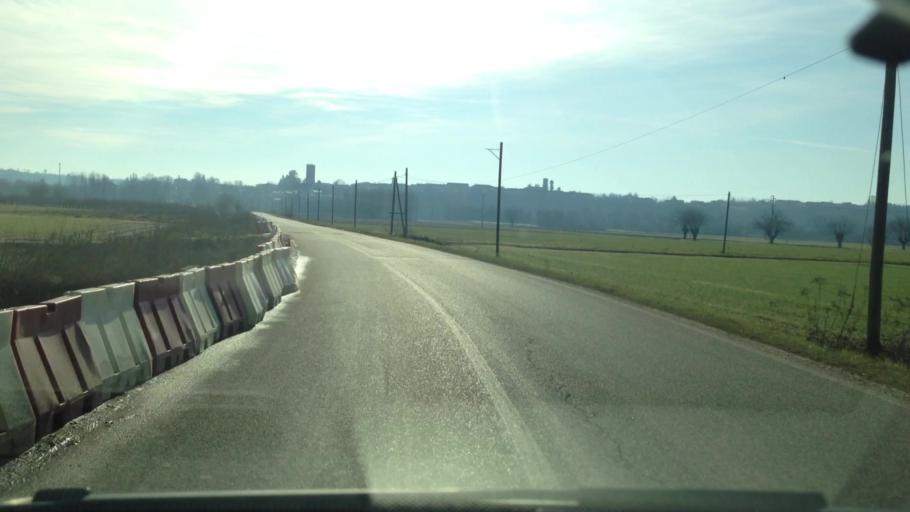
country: IT
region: Piedmont
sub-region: Provincia di Alessandria
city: Masio
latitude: 44.8807
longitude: 8.4092
